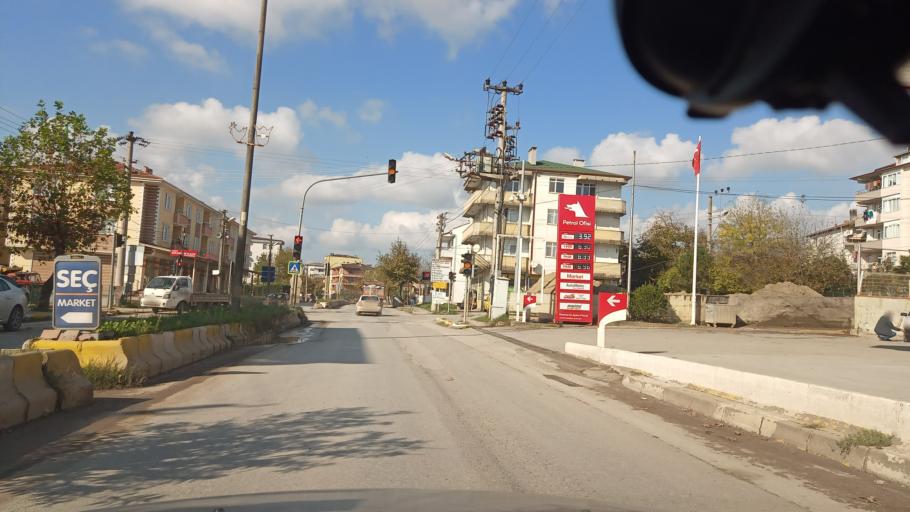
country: TR
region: Sakarya
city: Kaynarca
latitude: 41.0367
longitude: 30.3005
